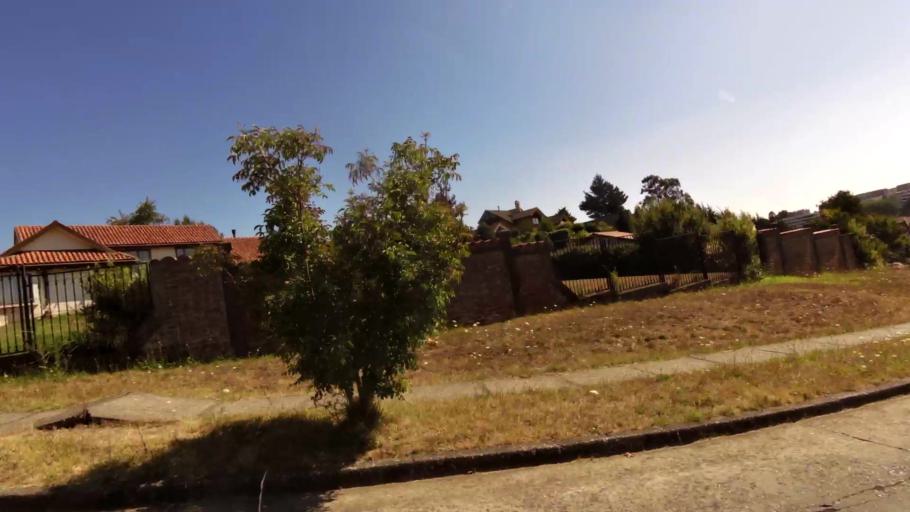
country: CL
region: Biobio
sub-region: Provincia de Concepcion
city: Concepcion
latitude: -36.7922
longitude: -73.0536
